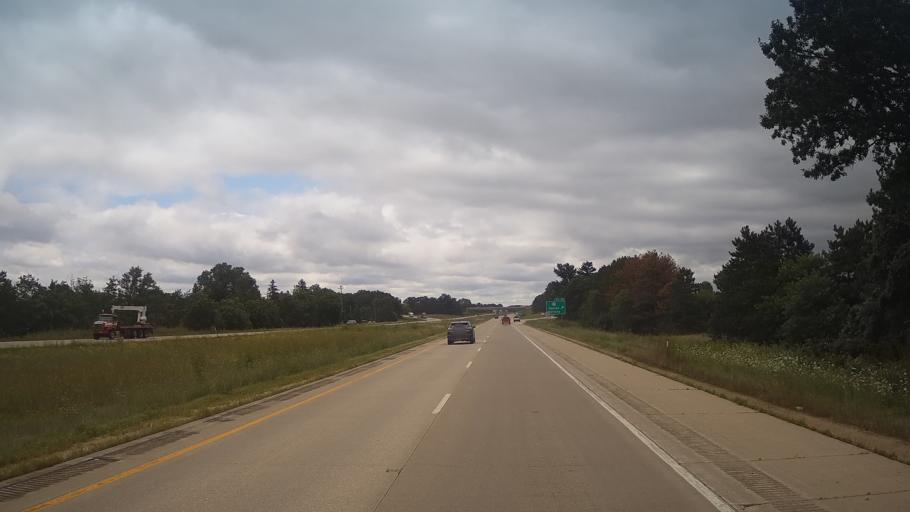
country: US
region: Wisconsin
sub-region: Monroe County
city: Sparta
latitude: 43.9186
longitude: -90.8307
